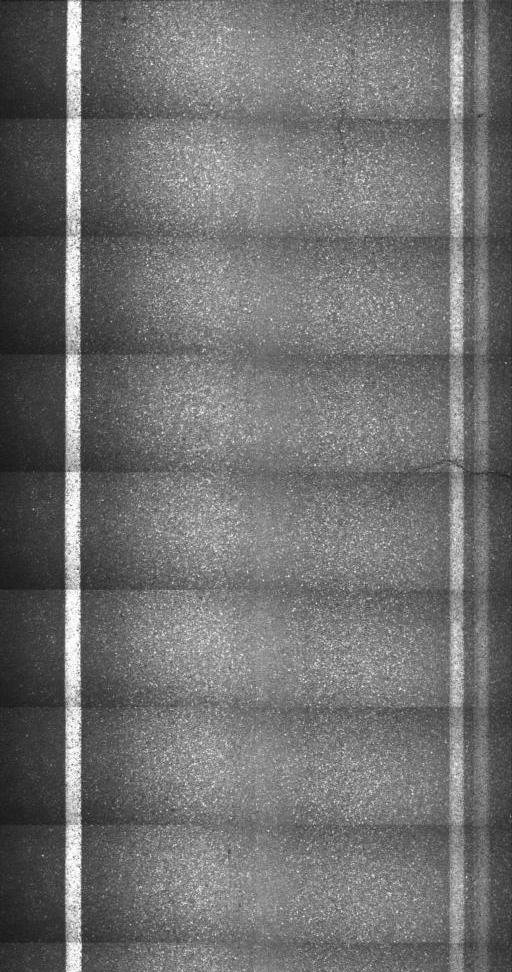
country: US
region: Vermont
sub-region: Orleans County
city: Newport
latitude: 44.9091
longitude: -72.0046
